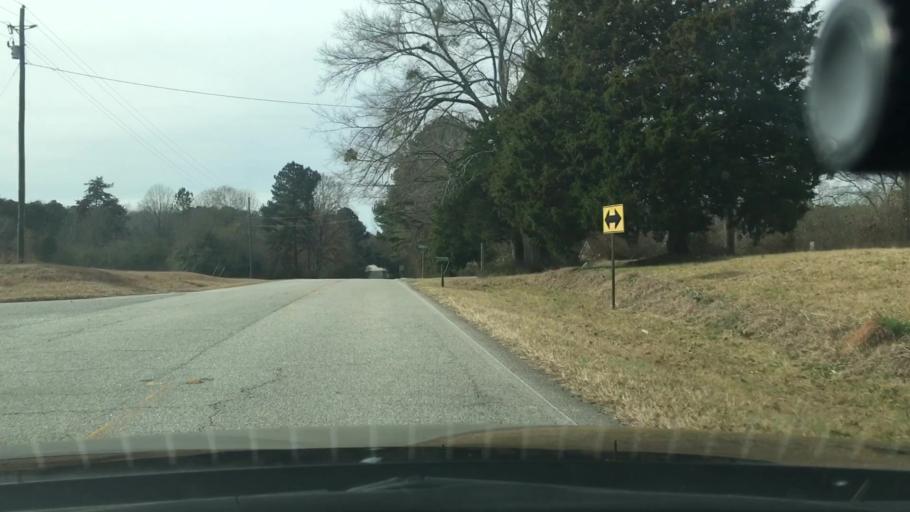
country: US
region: Georgia
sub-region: Coweta County
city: Senoia
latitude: 33.2865
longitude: -84.4386
